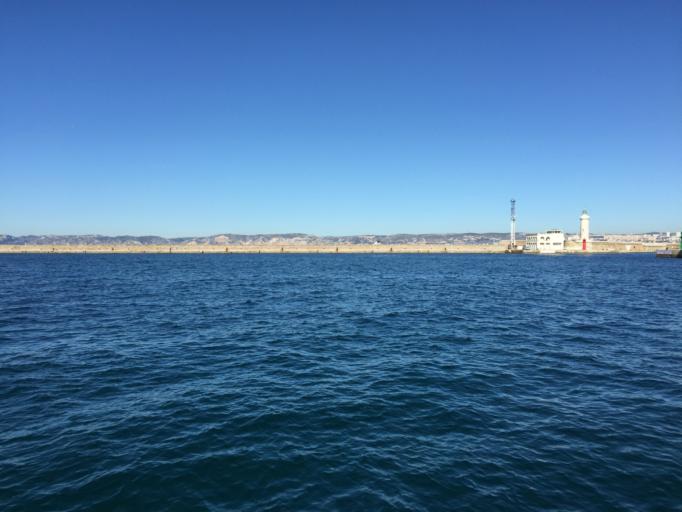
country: FR
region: Provence-Alpes-Cote d'Azur
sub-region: Departement des Bouches-du-Rhone
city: Marseille 02
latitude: 43.2961
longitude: 5.3587
